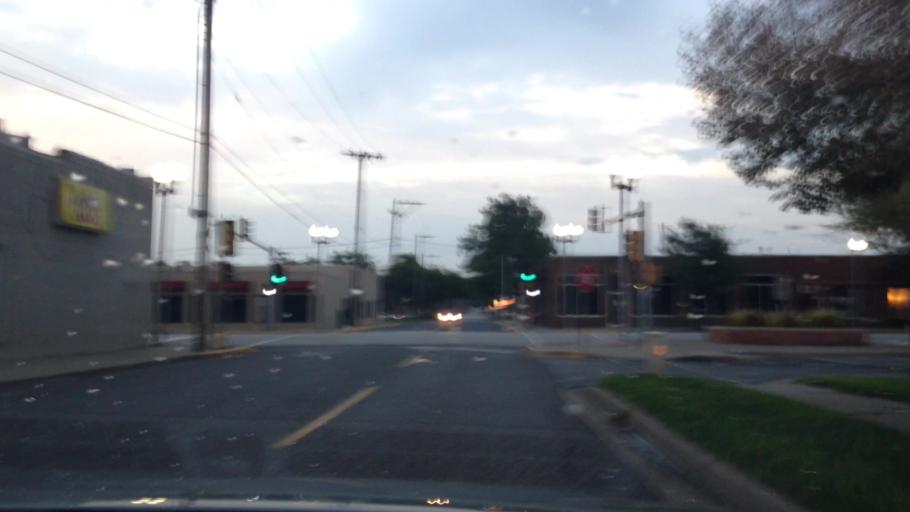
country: US
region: Missouri
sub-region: Clay County
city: North Kansas City
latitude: 39.1402
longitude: -94.5778
